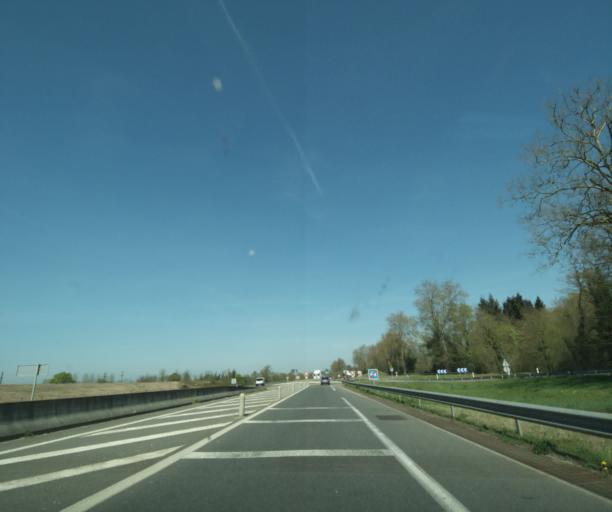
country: FR
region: Auvergne
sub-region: Departement de l'Allier
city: Trevol
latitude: 46.6241
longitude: 3.2868
